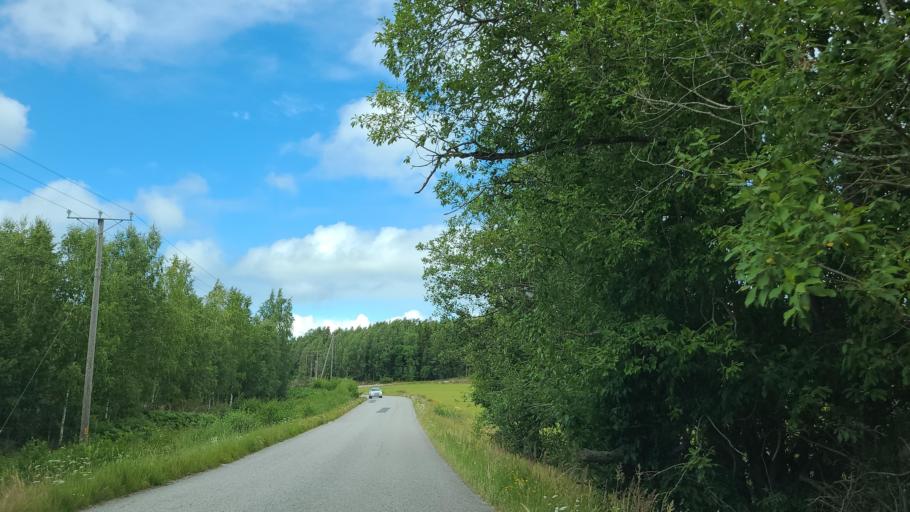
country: FI
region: Varsinais-Suomi
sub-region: Aboland-Turunmaa
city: Nagu
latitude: 60.1729
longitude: 21.9798
